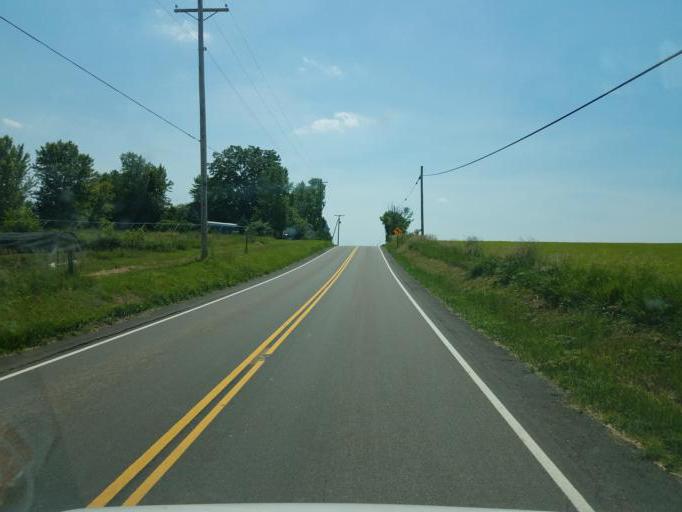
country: US
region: Ohio
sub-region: Knox County
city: Danville
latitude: 40.4576
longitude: -82.2580
